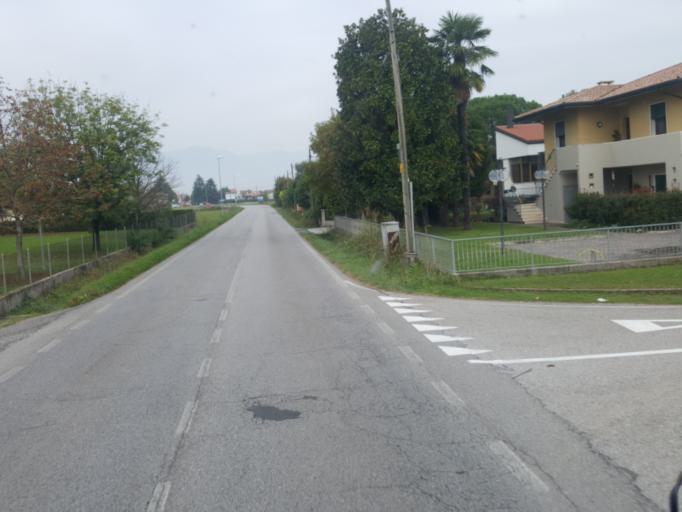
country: IT
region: Veneto
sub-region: Provincia di Treviso
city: Castello di Godego
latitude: 45.6981
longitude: 11.8756
